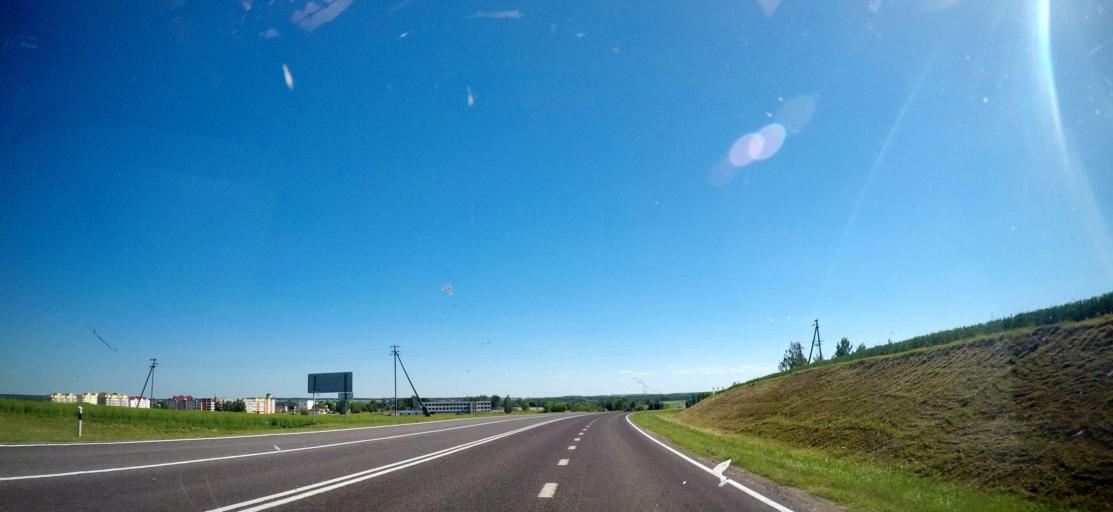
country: BY
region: Grodnenskaya
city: Vyalikaya Byerastavitsa
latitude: 53.2067
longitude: 24.0061
